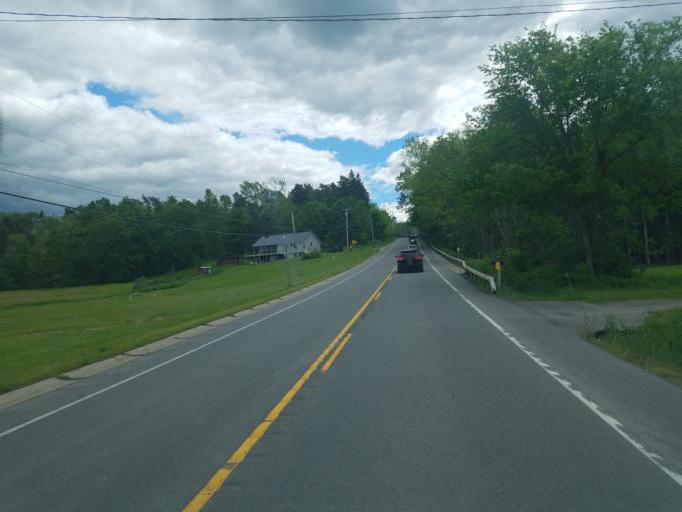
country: US
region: New York
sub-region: Herkimer County
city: Mohawk
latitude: 42.9771
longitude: -75.0107
